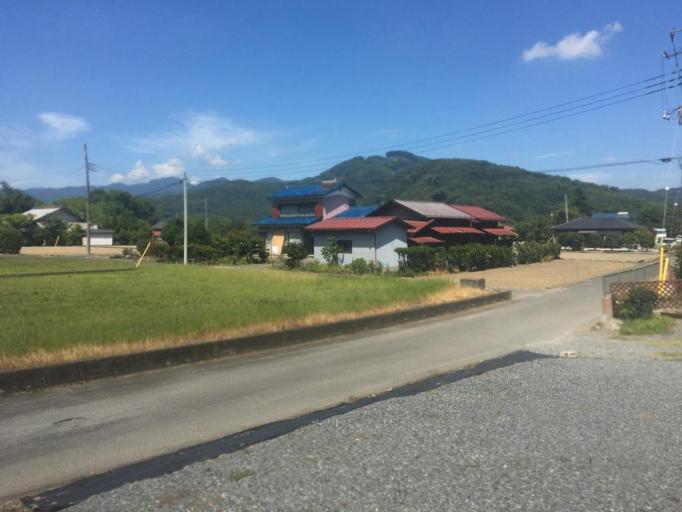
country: JP
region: Saitama
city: Yorii
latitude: 36.0801
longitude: 139.1149
